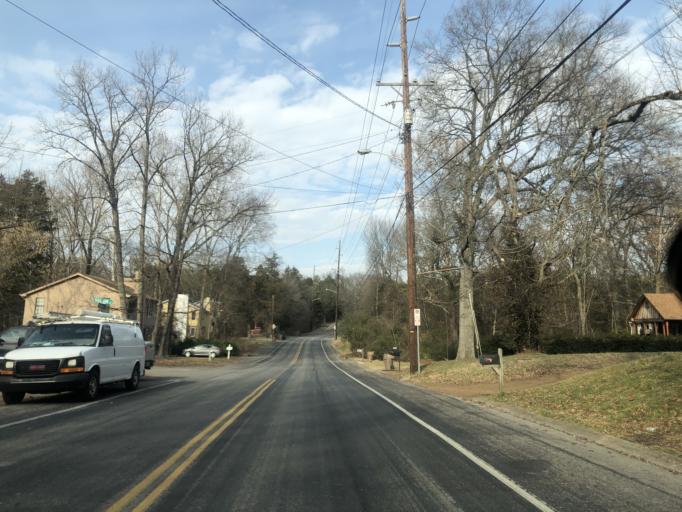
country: US
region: Tennessee
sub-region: Davidson County
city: Oak Hill
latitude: 36.1059
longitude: -86.7040
